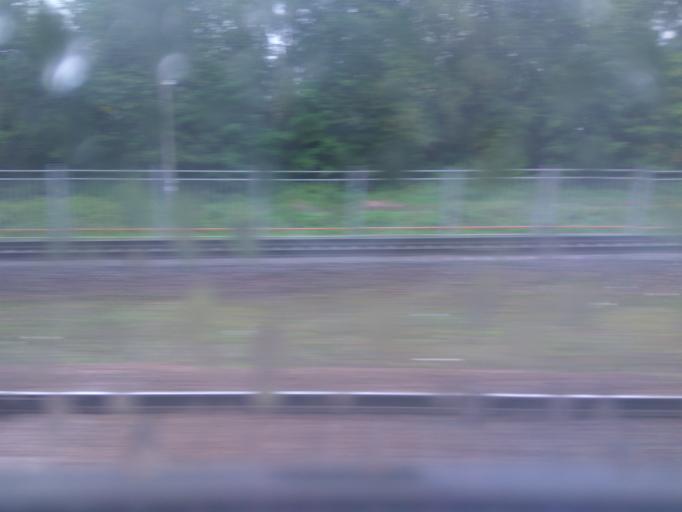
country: RU
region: Moscow
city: Zagor'ye
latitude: 55.5650
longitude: 37.6698
